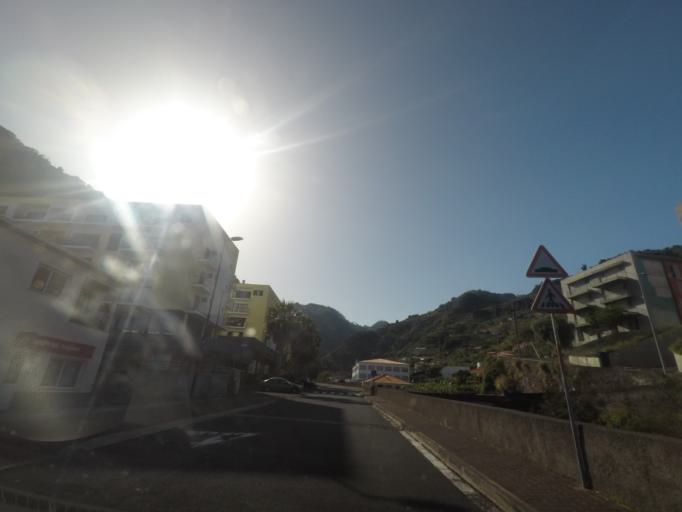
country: PT
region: Madeira
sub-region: Santa Cruz
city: Santa Cruz
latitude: 32.6895
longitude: -16.7958
